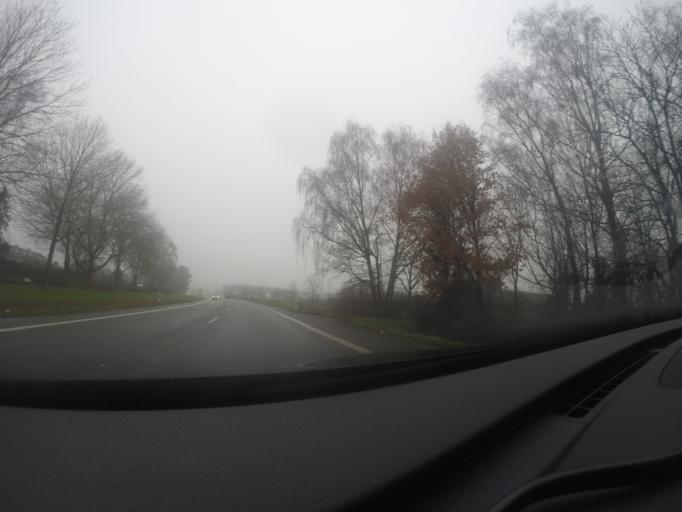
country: DE
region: North Rhine-Westphalia
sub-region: Regierungsbezirk Dusseldorf
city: Bocholt
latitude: 51.8582
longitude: 6.5866
